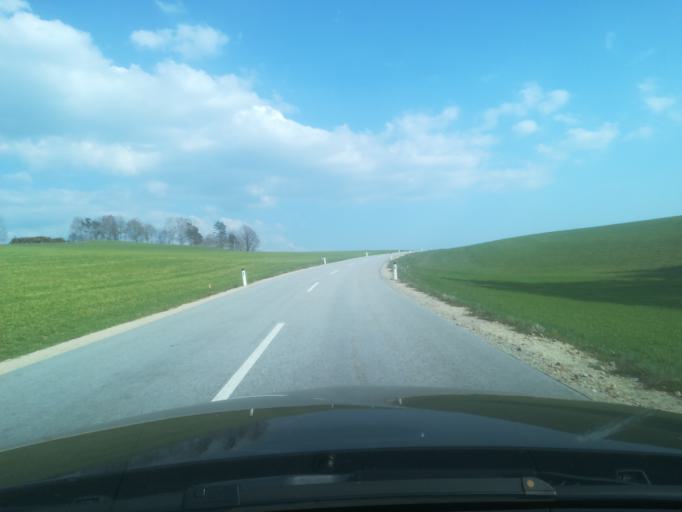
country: AT
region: Upper Austria
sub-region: Politischer Bezirk Perg
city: Perg
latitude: 48.3602
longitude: 14.6591
